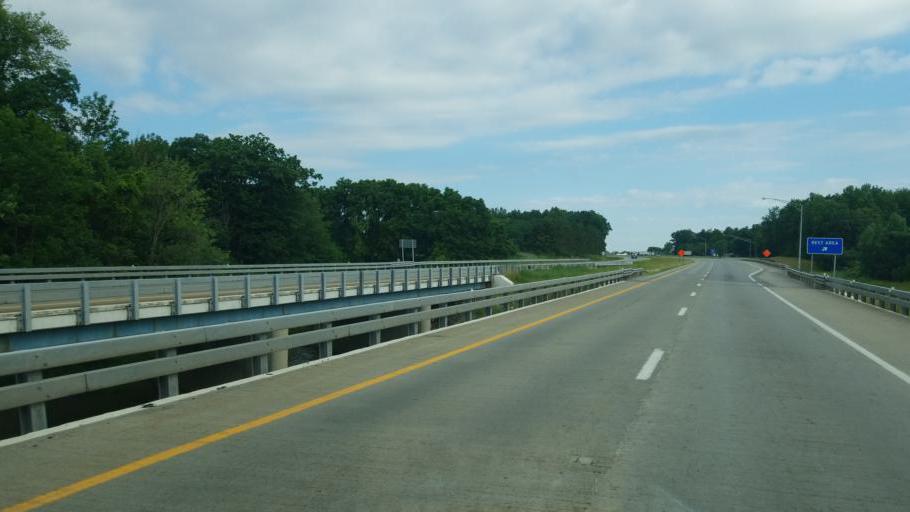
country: US
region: Ohio
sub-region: Wyandot County
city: Carey
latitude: 40.9169
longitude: -83.3540
